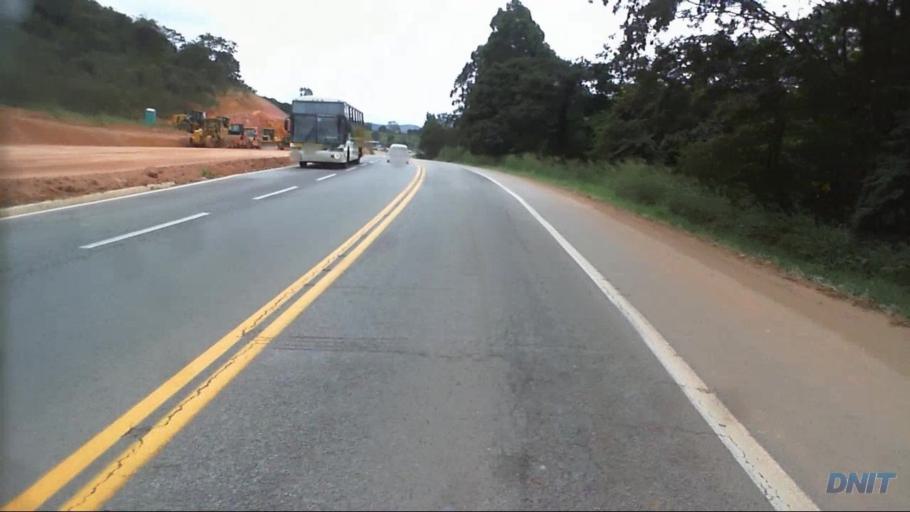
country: BR
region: Minas Gerais
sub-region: Caete
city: Caete
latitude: -19.7442
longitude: -43.5499
